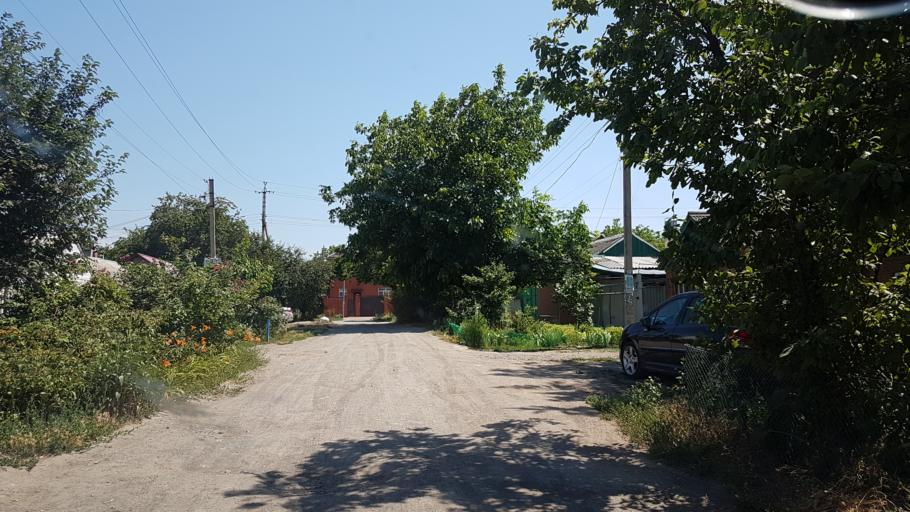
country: RU
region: Rostov
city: Severnyy
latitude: 47.2690
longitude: 39.7086
